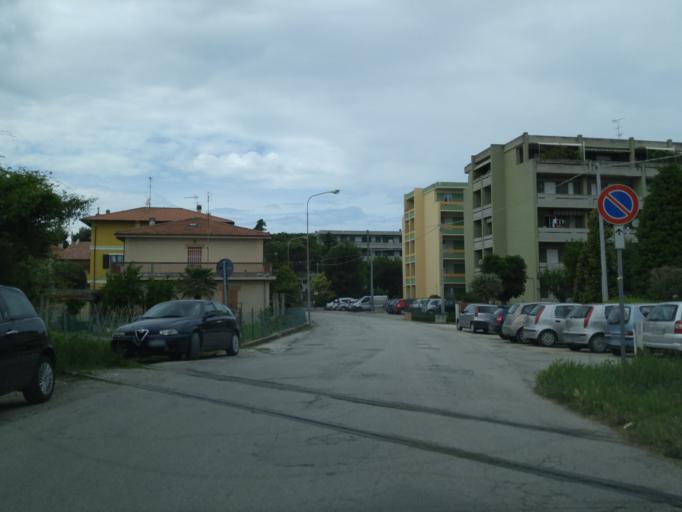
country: IT
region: The Marches
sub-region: Provincia di Pesaro e Urbino
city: Fano
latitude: 43.8326
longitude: 13.0292
